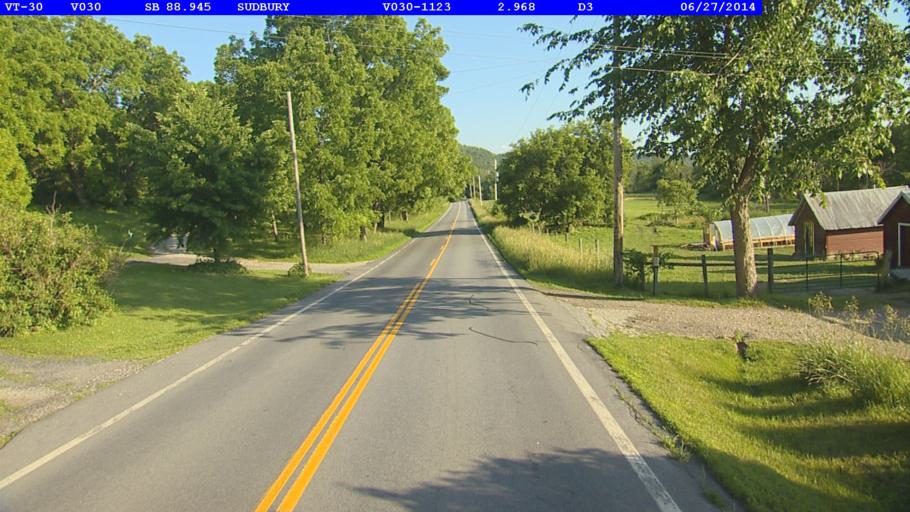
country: US
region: Vermont
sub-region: Rutland County
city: Brandon
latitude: 43.7907
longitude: -73.2042
